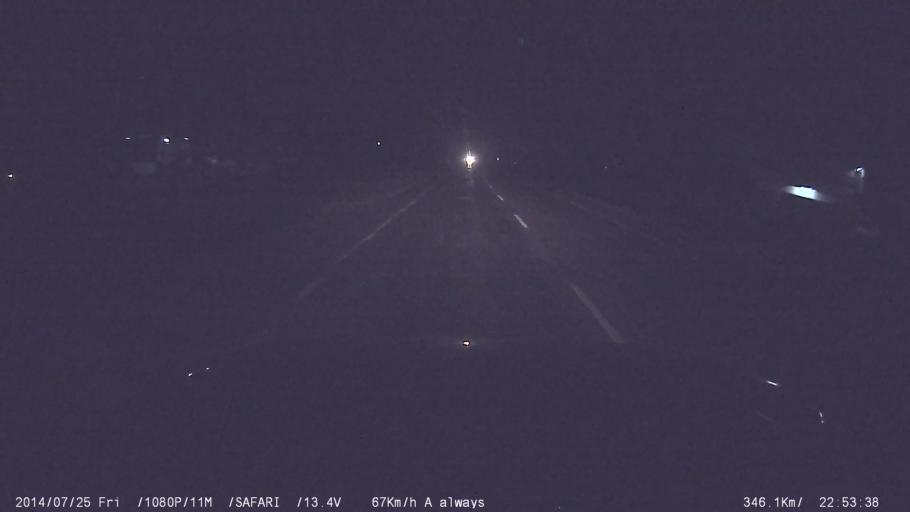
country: IN
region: Tamil Nadu
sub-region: Coimbatore
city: Irugur
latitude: 11.0013
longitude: 77.0666
